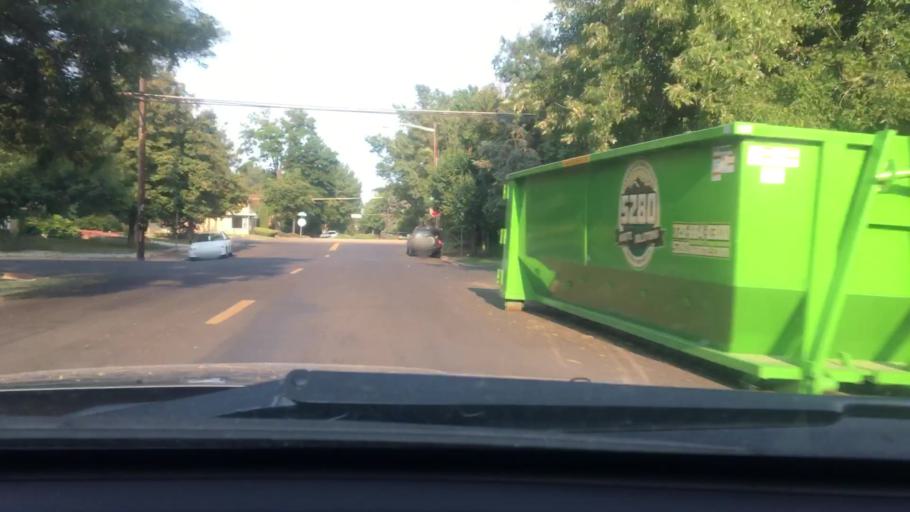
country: US
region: Colorado
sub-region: Arapahoe County
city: Glendale
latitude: 39.7194
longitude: -104.9416
